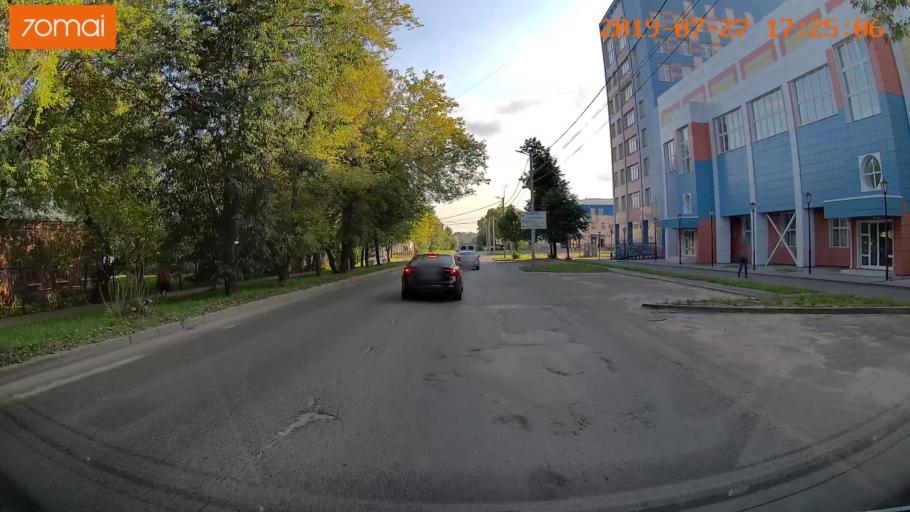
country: RU
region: Ivanovo
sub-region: Gorod Ivanovo
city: Ivanovo
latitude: 57.0183
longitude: 40.9582
